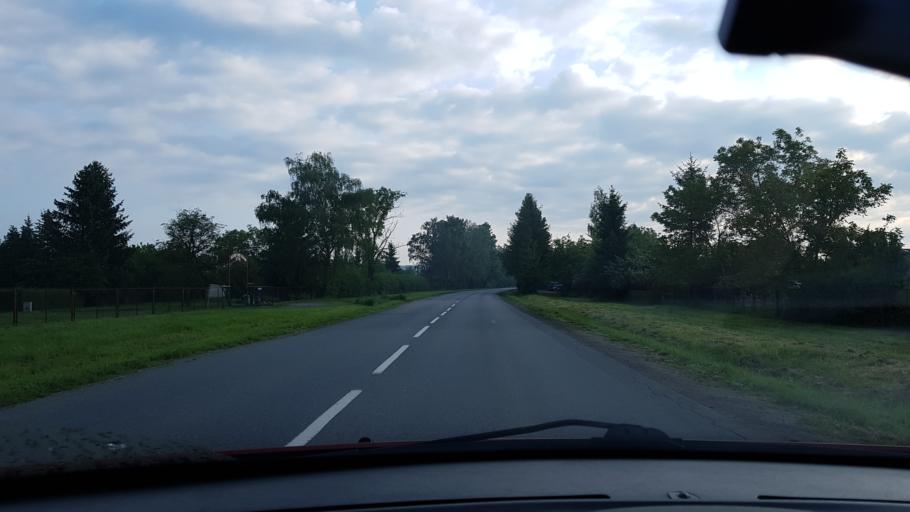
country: PL
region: Lower Silesian Voivodeship
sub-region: Powiat zabkowicki
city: Zabkowice Slaskie
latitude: 50.6035
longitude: 16.8205
